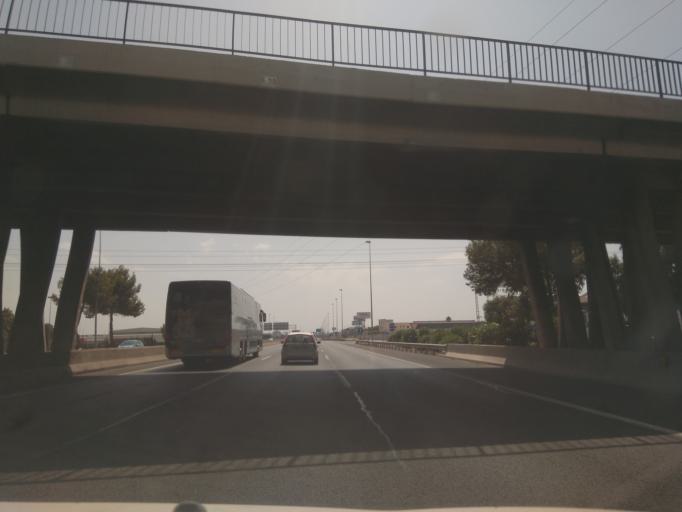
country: ES
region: Valencia
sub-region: Provincia de Valencia
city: Catarroja
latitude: 39.3875
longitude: -0.3958
